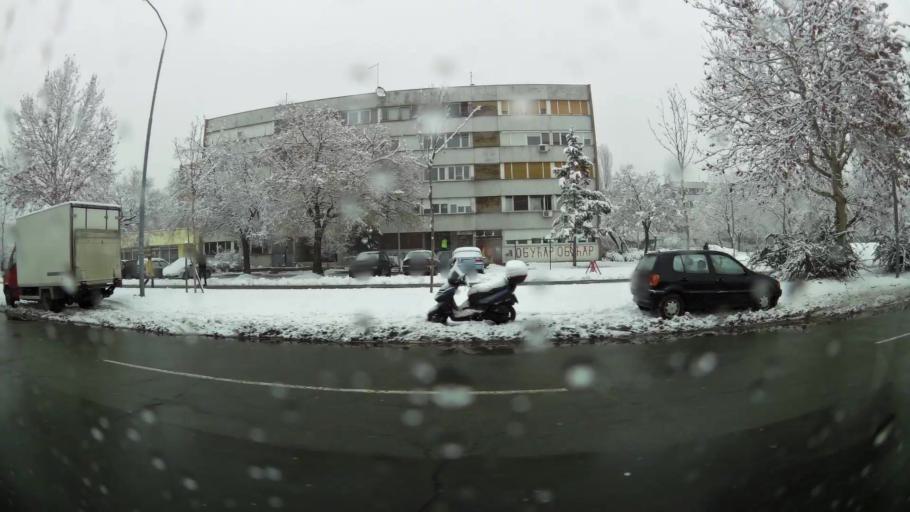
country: RS
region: Central Serbia
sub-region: Belgrade
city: Cukarica
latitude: 44.7933
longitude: 20.3748
